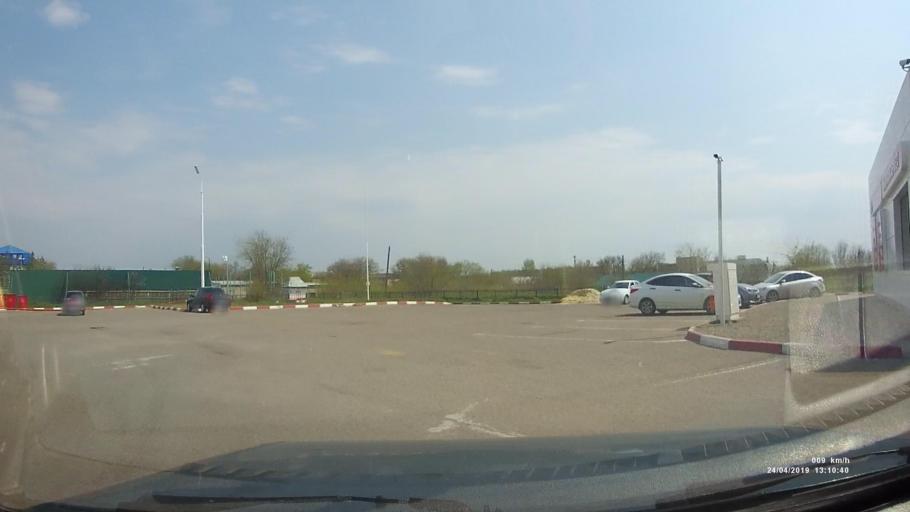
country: RU
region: Kalmykiya
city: Elista
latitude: 46.3116
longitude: 44.2941
